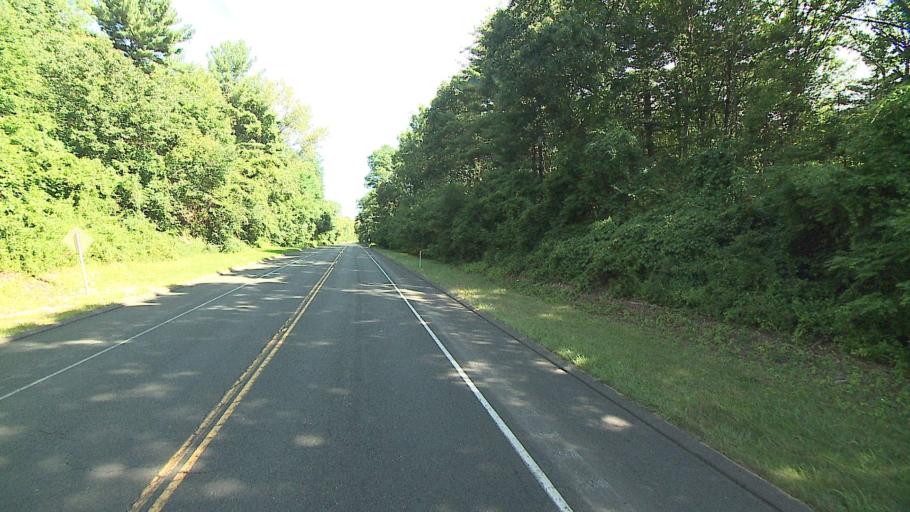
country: US
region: Connecticut
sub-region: Hartford County
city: Tariffville
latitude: 41.9024
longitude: -72.7470
